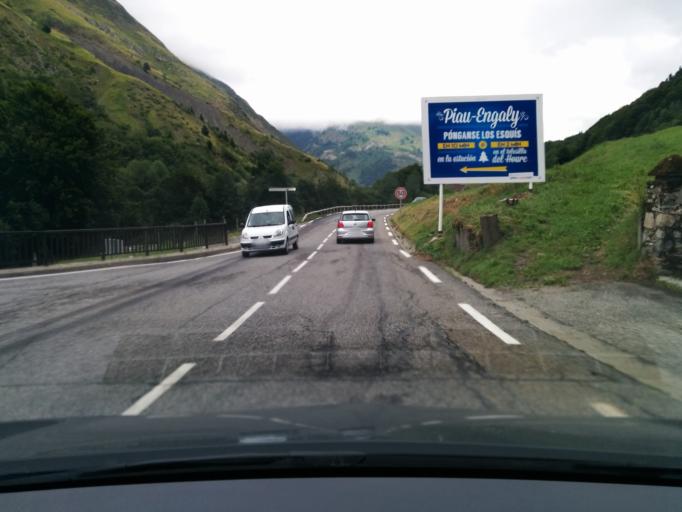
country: FR
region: Midi-Pyrenees
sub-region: Departement des Hautes-Pyrenees
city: Saint-Lary-Soulan
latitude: 42.7800
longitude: 0.1942
